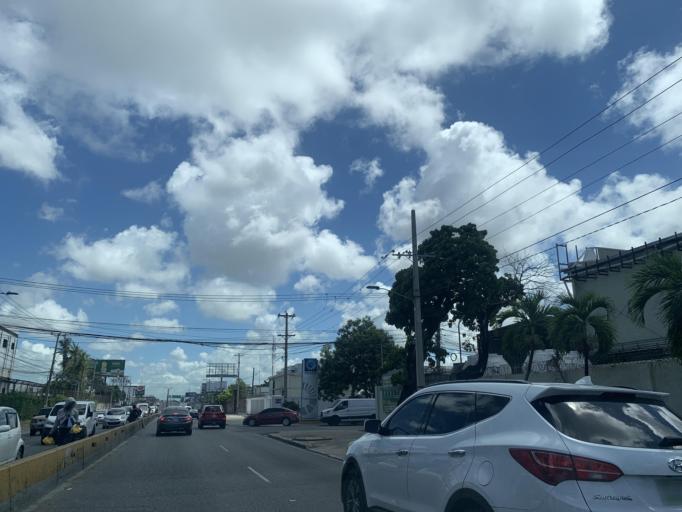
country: DO
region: Nacional
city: Ensanche Luperon
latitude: 18.4956
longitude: -69.9152
